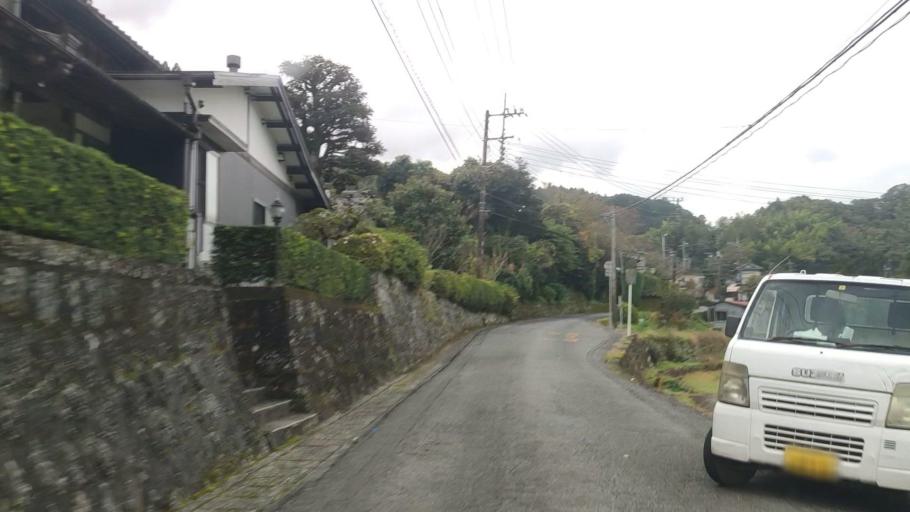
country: JP
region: Shizuoka
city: Ito
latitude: 34.9137
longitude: 138.9774
